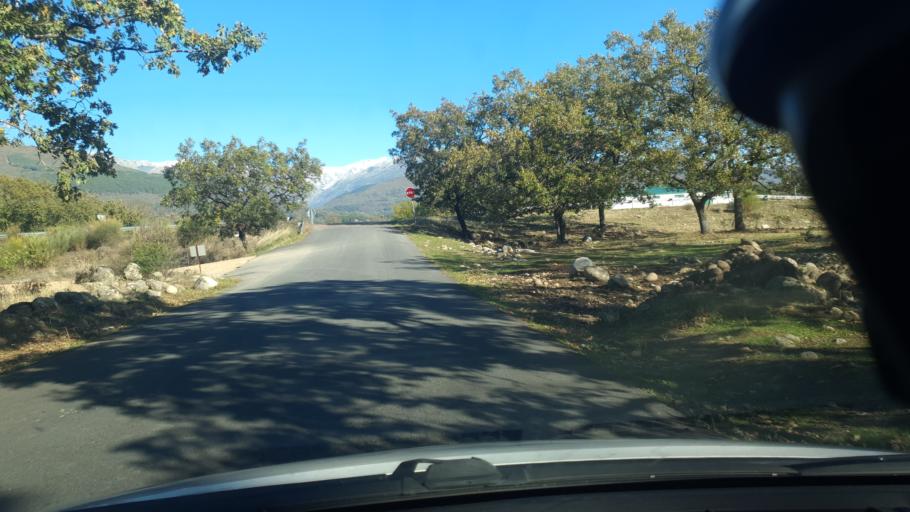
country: ES
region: Castille and Leon
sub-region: Provincia de Avila
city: Candeleda
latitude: 40.1399
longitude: -5.2588
